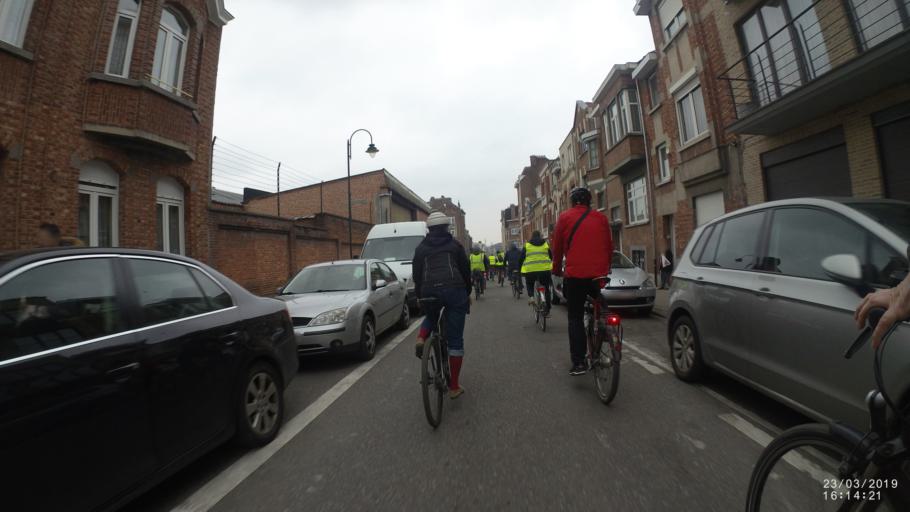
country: BE
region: Brussels Capital
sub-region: Bruxelles-Capitale
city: Brussels
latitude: 50.8746
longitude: 4.3391
